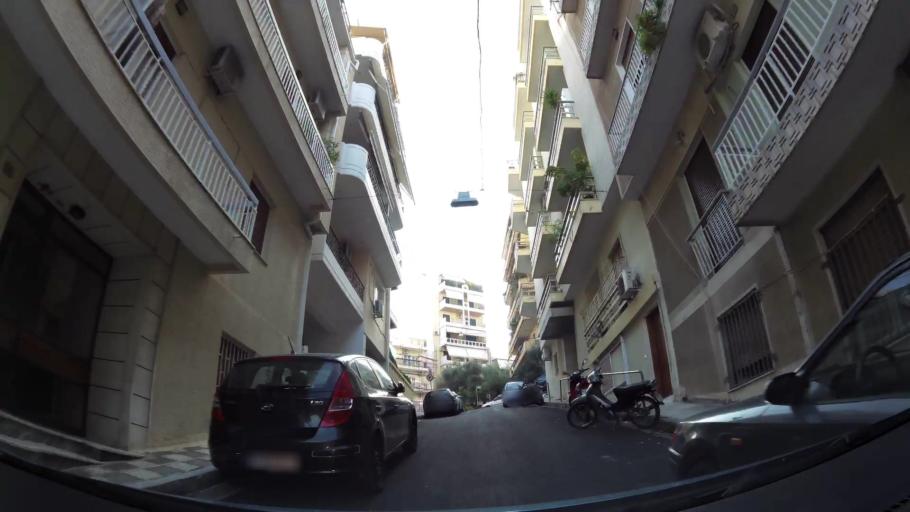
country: GR
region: Attica
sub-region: Nomarchia Athinas
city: Kaisariani
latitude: 37.9719
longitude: 23.7690
